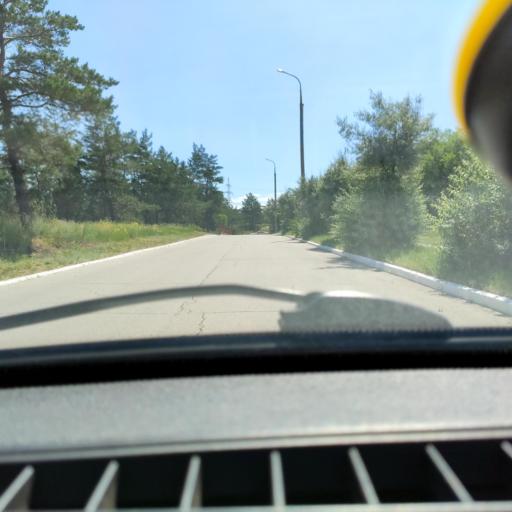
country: RU
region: Samara
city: Zhigulevsk
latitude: 53.4902
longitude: 49.5145
